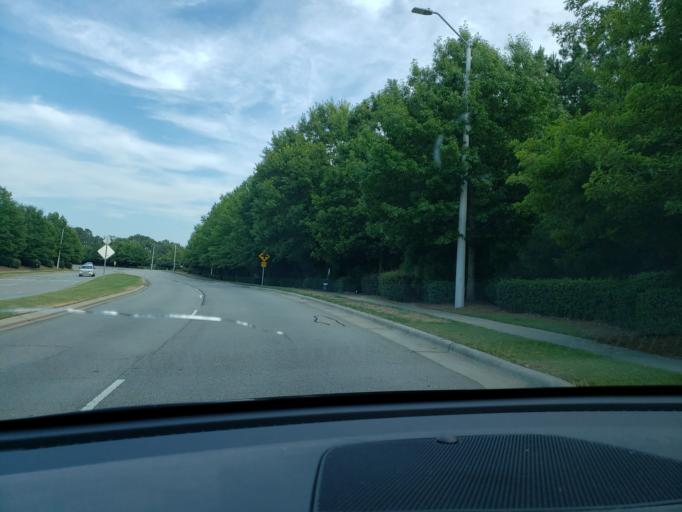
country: US
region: North Carolina
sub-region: Wake County
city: Green Level
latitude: 35.8233
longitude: -78.9095
